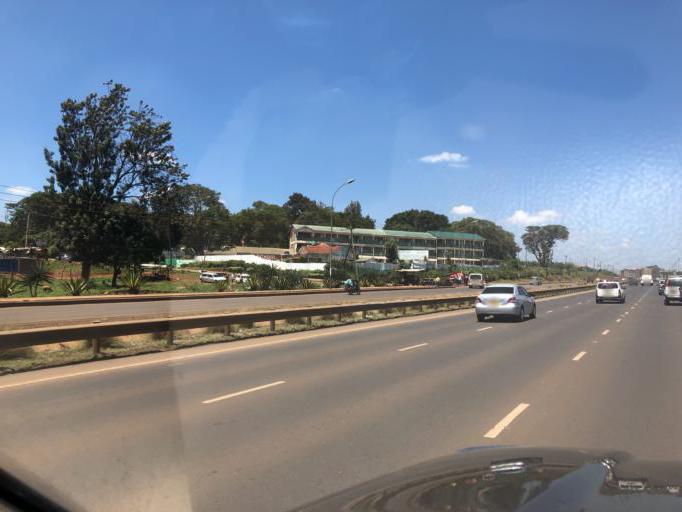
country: KE
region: Kiambu
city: Kiambu
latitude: -1.2120
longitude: 36.9044
